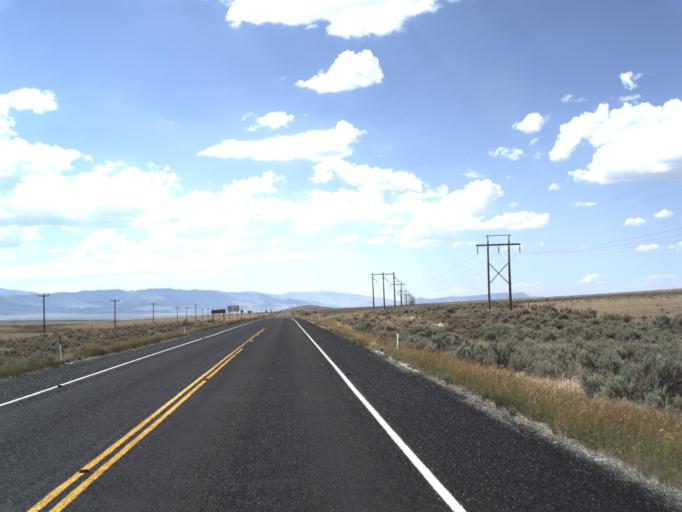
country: US
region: Idaho
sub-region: Minidoka County
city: Rupert
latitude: 41.9922
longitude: -113.1864
